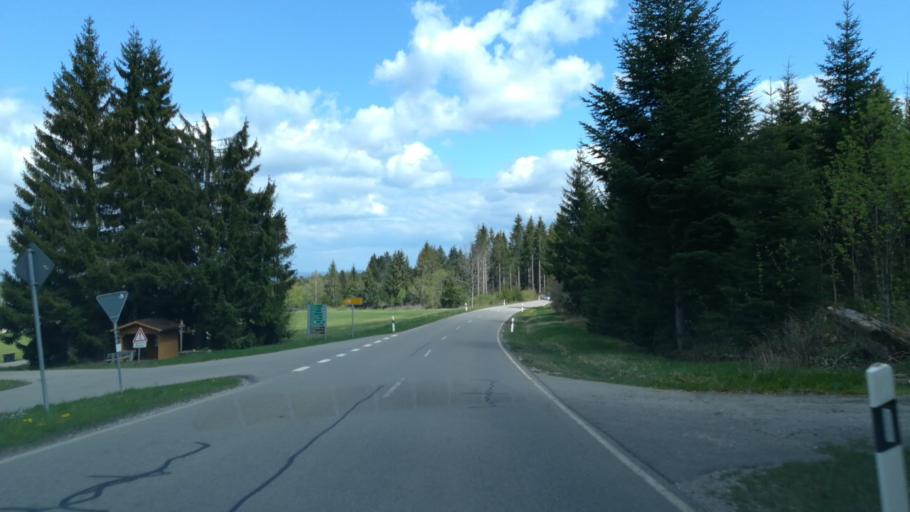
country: DE
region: Baden-Wuerttemberg
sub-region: Freiburg Region
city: Lenzkirch
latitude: 47.8300
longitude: 8.2486
